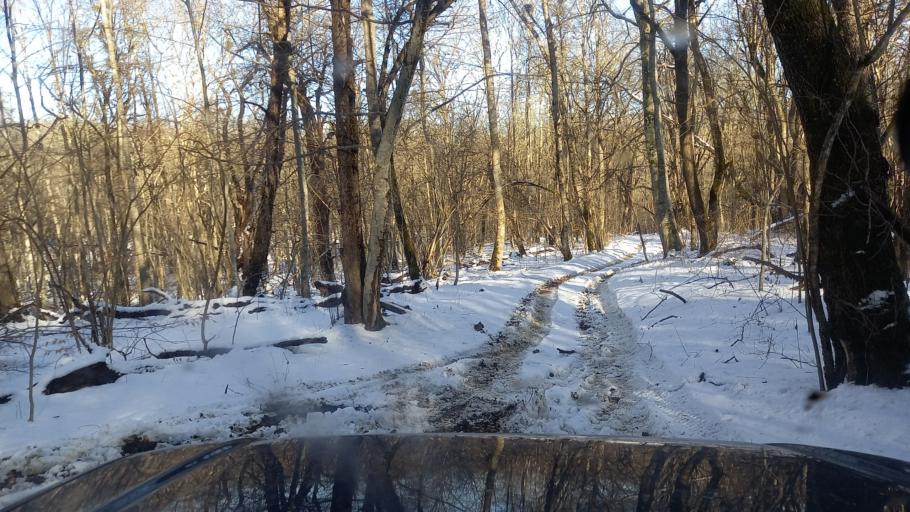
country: RU
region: Adygeya
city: Kamennomostskiy
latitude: 44.2131
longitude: 40.1326
